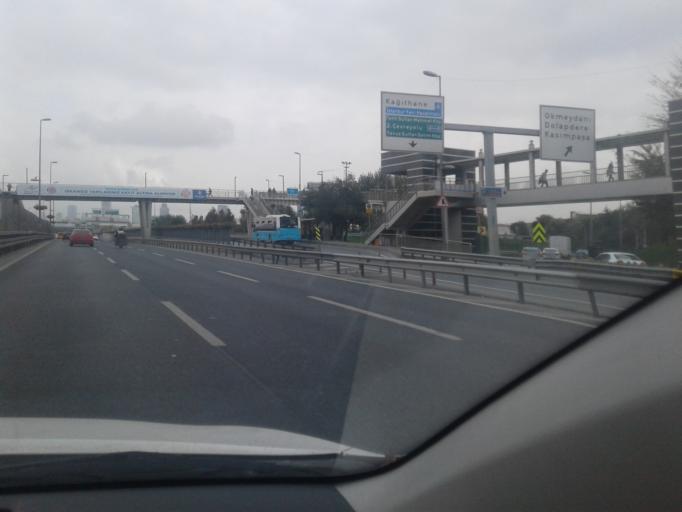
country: TR
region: Istanbul
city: Sisli
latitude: 41.0549
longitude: 28.9586
